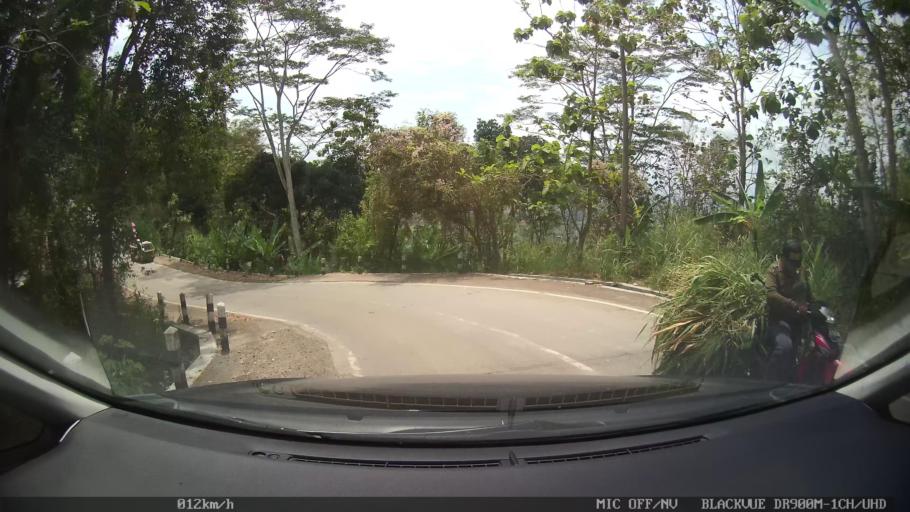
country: ID
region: Central Java
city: Candi Prambanan
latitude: -7.7911
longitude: 110.5187
